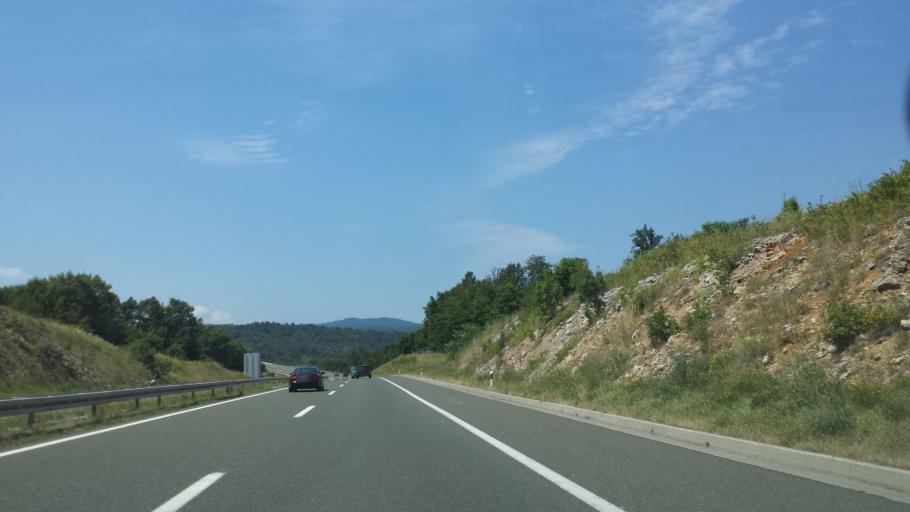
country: HR
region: Karlovacka
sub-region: Grad Ogulin
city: Ogulin
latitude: 45.4005
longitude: 15.2273
